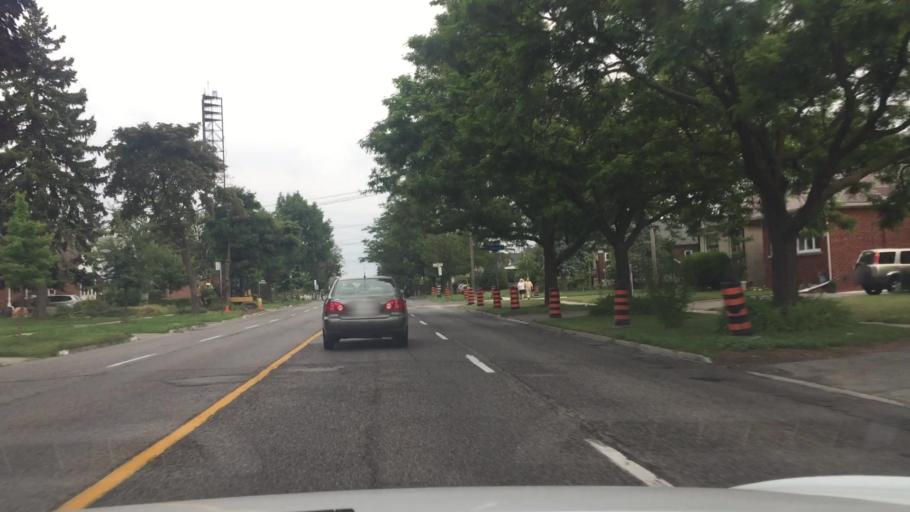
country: CA
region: Ontario
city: Scarborough
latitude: 43.7336
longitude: -79.3008
